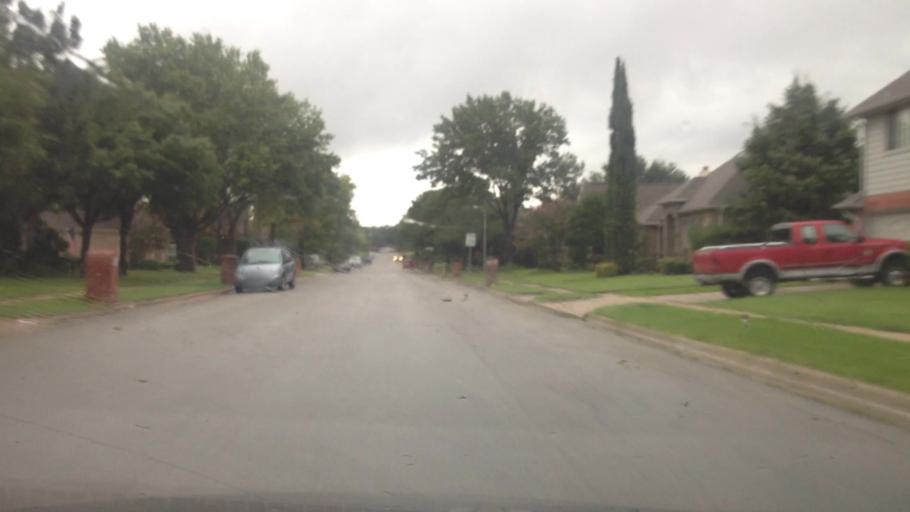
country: US
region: Texas
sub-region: Tarrant County
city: Colleyville
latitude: 32.8687
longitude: -97.1751
